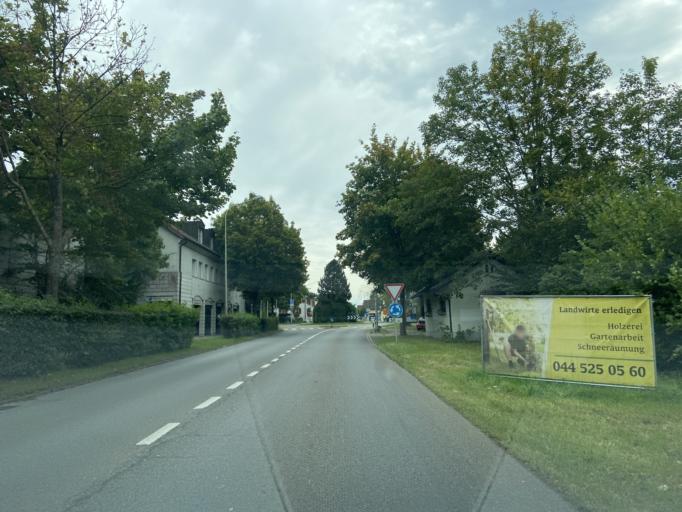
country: CH
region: Zurich
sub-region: Bezirk Pfaeffikon
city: Illnau / Unter-Illnau
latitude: 47.4093
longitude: 8.7253
